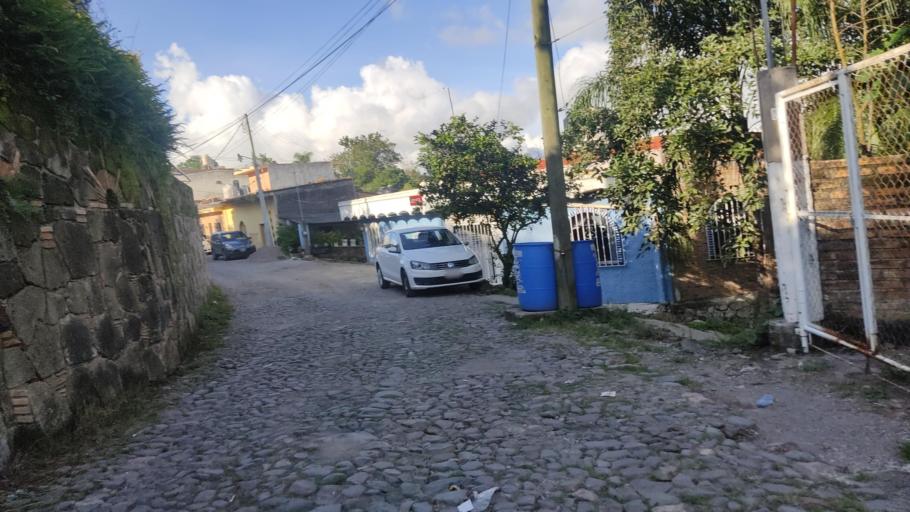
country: MX
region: Nayarit
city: Xalisco
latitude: 21.4274
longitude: -104.8586
